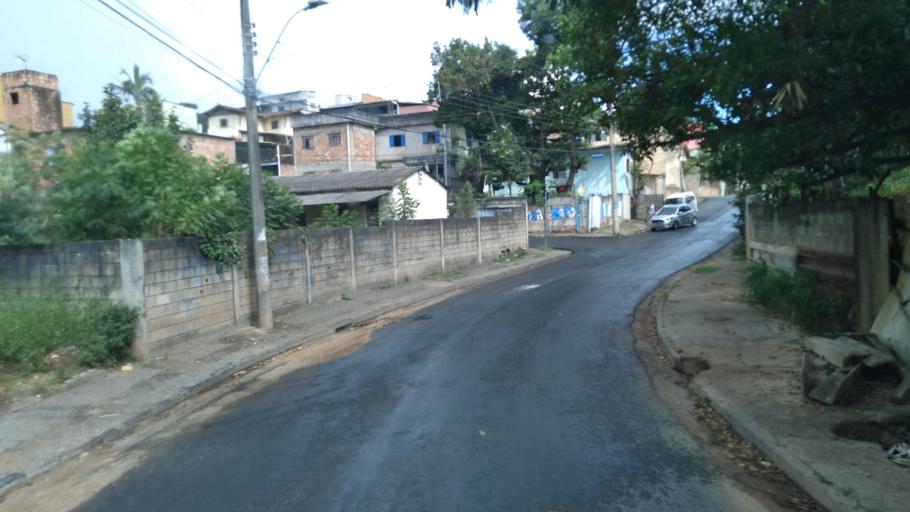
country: BR
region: Minas Gerais
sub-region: Contagem
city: Contagem
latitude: -19.9204
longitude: -44.0131
